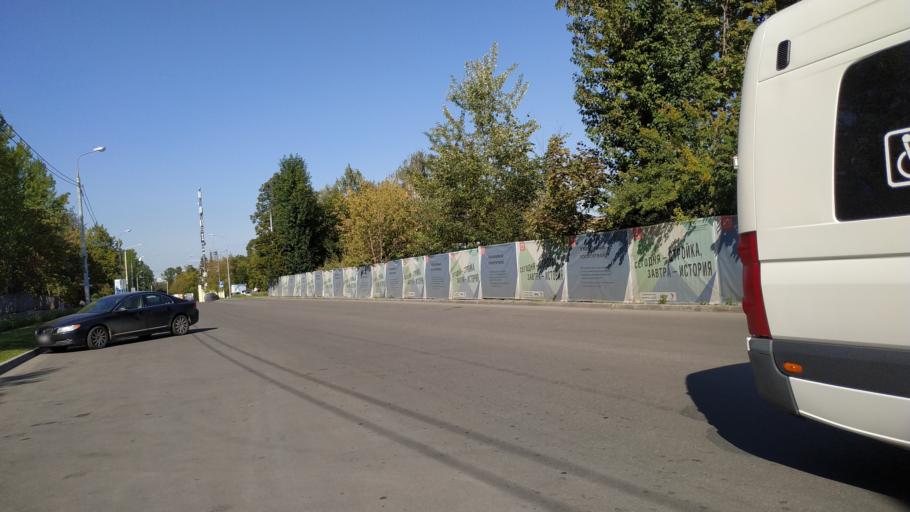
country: RU
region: Moscow
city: Ostankinskiy
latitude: 55.8277
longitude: 37.6218
